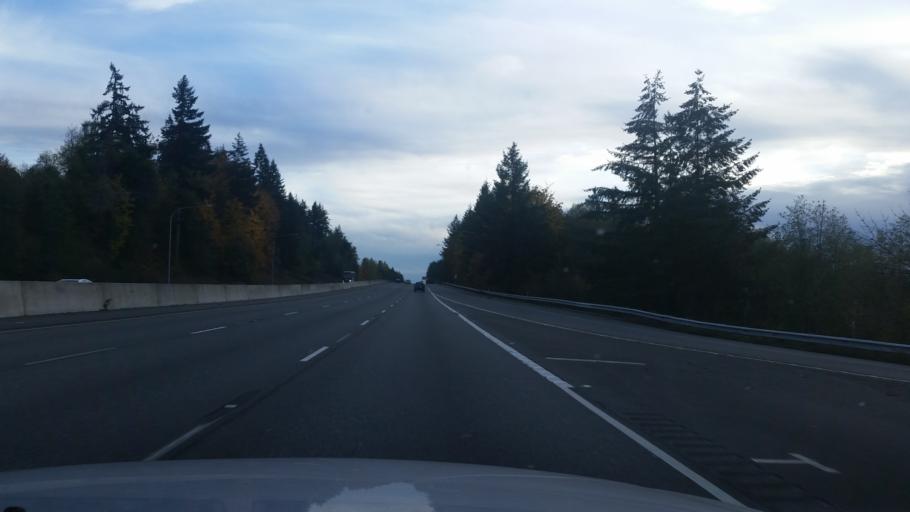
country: US
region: Washington
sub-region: Thurston County
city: Tenino
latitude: 46.8936
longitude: -122.9620
